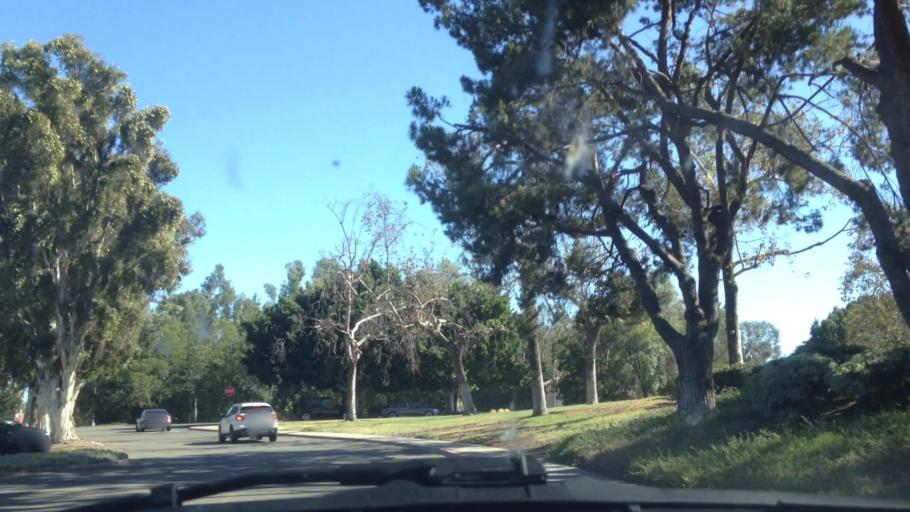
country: US
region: California
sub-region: Orange County
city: Brea
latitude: 33.9139
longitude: -117.8850
